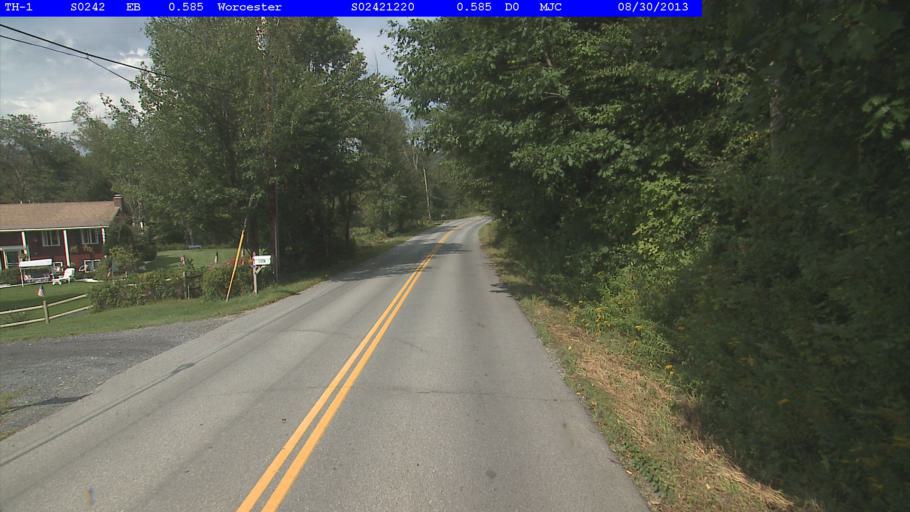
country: US
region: Vermont
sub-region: Washington County
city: Montpelier
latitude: 44.3764
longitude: -72.5413
